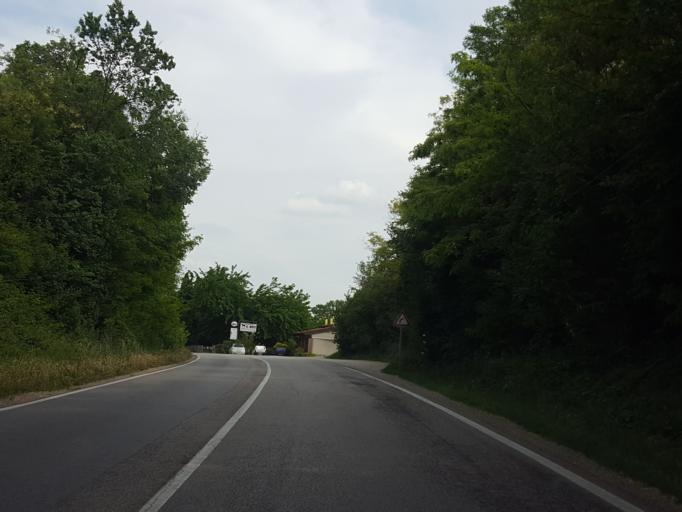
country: IT
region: Veneto
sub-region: Provincia di Vicenza
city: Orgiano
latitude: 45.3510
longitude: 11.4460
